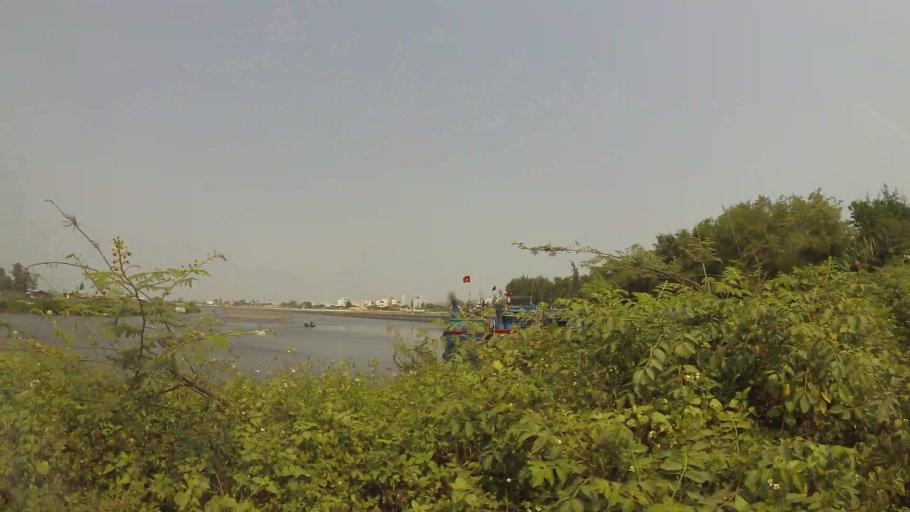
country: VN
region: Da Nang
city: Ngu Hanh Son
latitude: 16.0162
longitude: 108.2488
